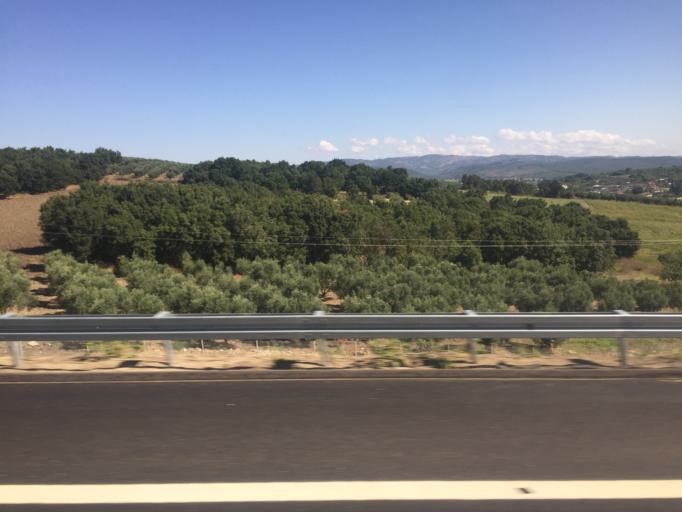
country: TR
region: Bursa
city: Gorukle
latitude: 40.2434
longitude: 28.7663
